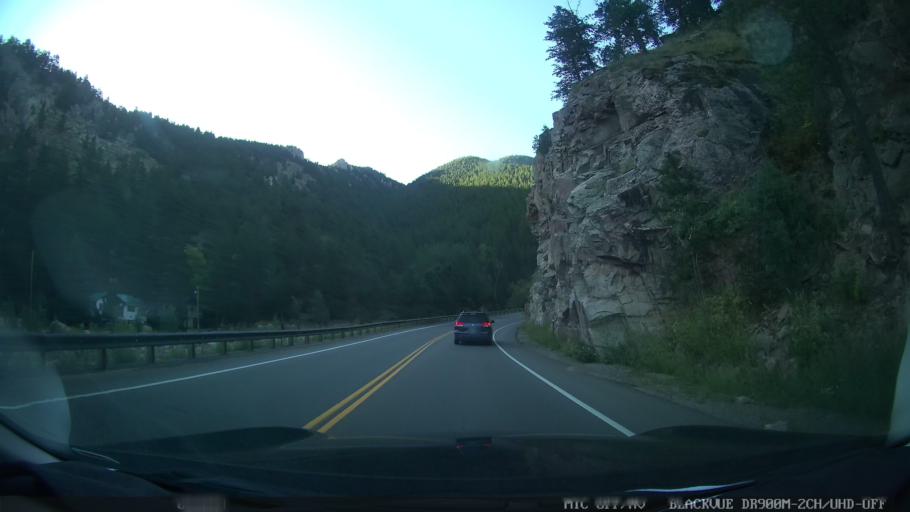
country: US
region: Colorado
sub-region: Larimer County
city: Estes Park
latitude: 40.4304
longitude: -105.3418
